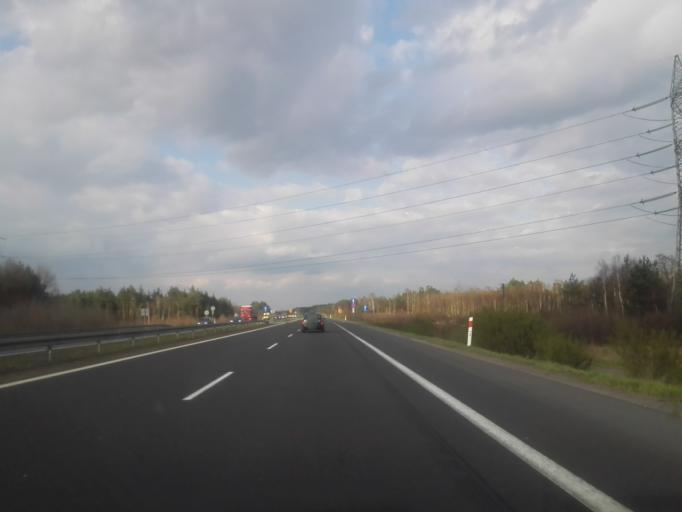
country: PL
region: Silesian Voivodeship
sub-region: Powiat czestochowski
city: Klomnice
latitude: 51.0290
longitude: 19.3292
